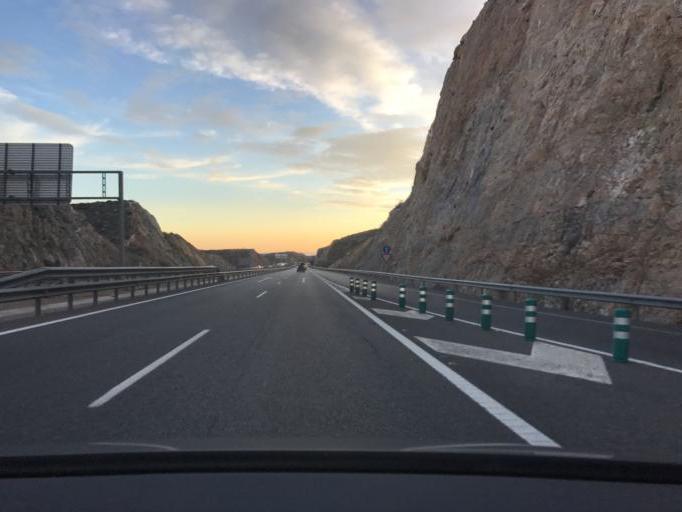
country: ES
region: Andalusia
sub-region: Provincia de Almeria
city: Huercal de Almeria
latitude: 36.8714
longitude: -2.4617
